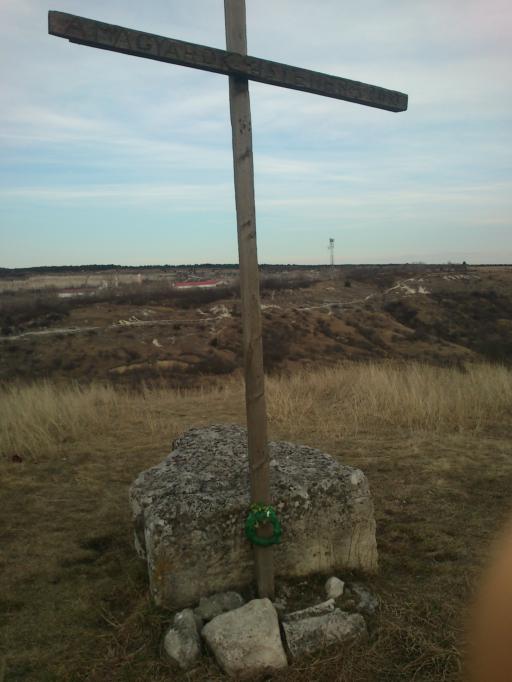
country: HU
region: Pest
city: Soskut
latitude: 47.4132
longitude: 18.8269
